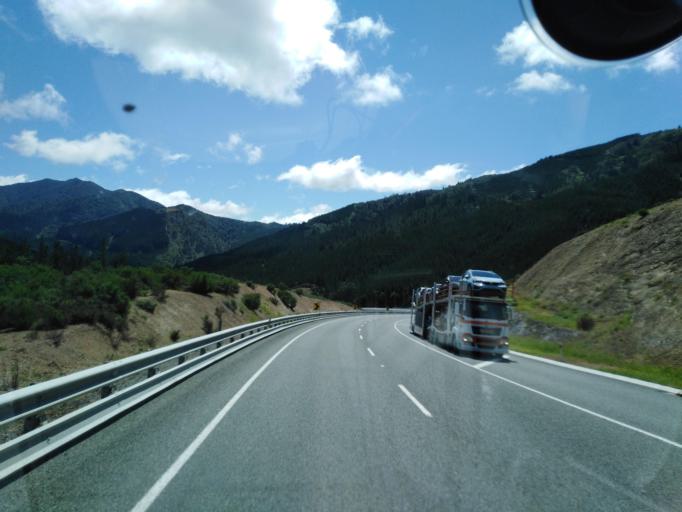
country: NZ
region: Nelson
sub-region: Nelson City
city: Nelson
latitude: -41.1863
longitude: 173.5562
